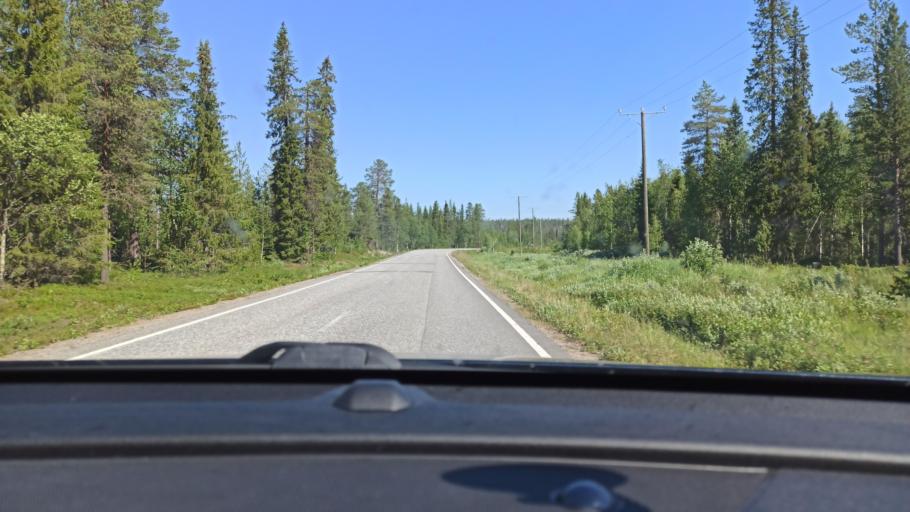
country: FI
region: Lapland
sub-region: Tunturi-Lappi
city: Kolari
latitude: 67.6288
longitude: 24.1561
